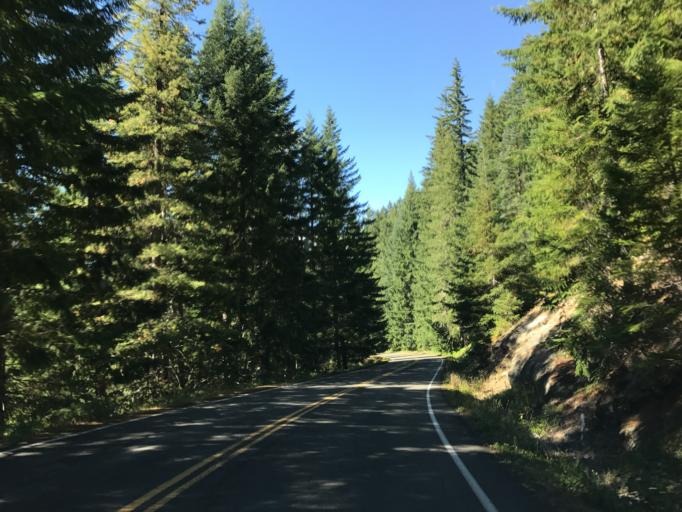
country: US
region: Washington
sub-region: Pierce County
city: Buckley
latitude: 46.7324
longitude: -121.6125
